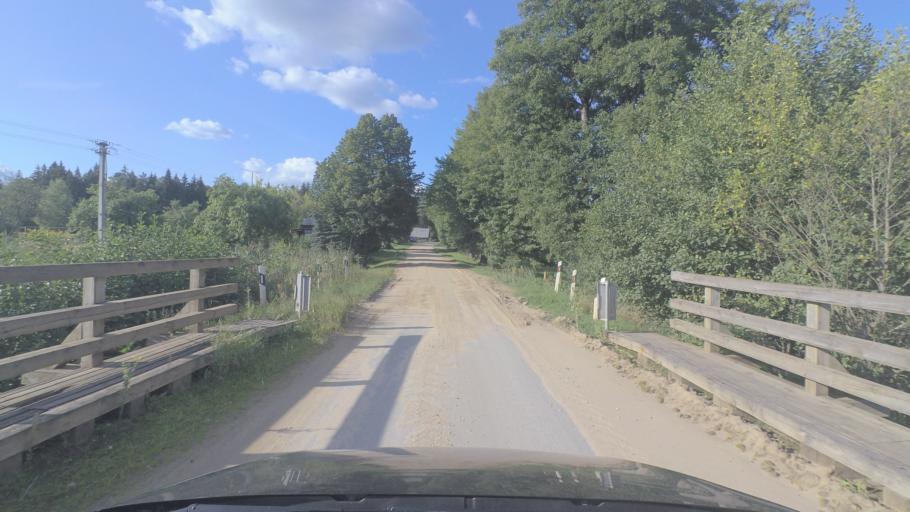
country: LT
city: Pabrade
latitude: 55.1497
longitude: 25.7651
